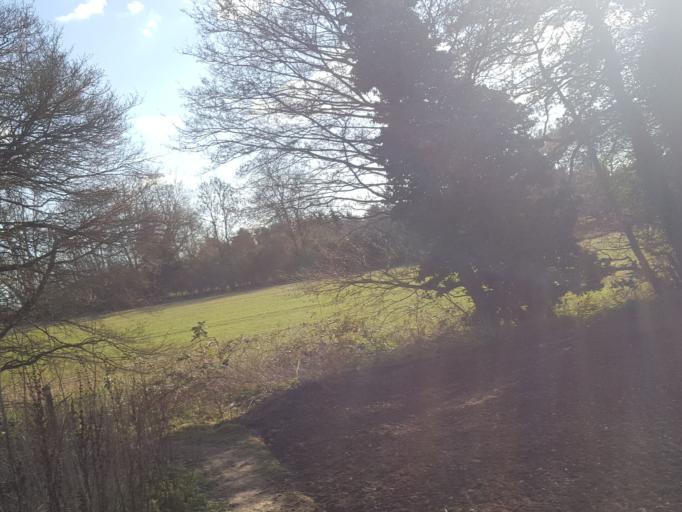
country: GB
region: England
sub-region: Essex
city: Little Clacton
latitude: 51.8633
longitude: 1.1135
